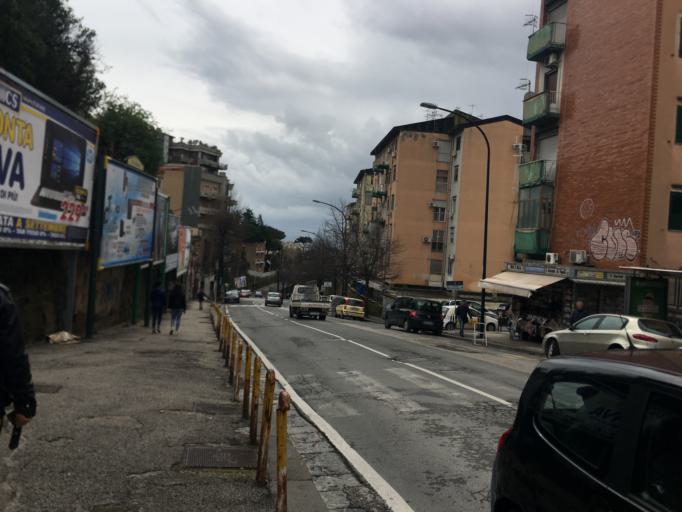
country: IT
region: Campania
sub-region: Provincia di Napoli
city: Napoli
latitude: 40.8609
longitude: 14.2247
